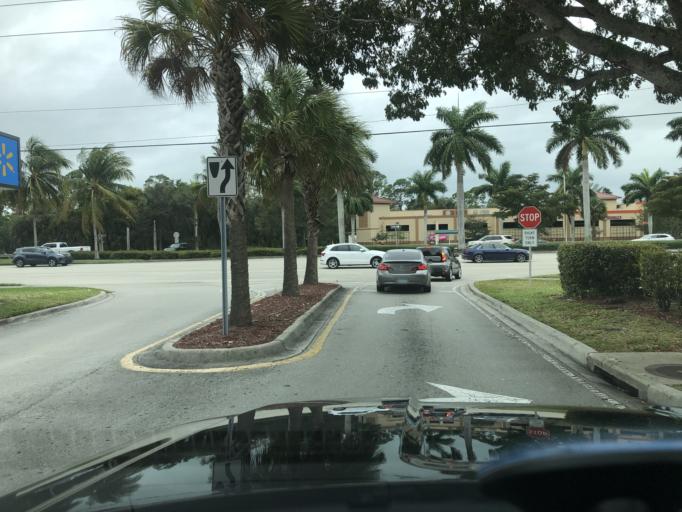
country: US
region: Florida
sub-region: Collier County
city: Naples
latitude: 26.1243
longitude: -81.7629
